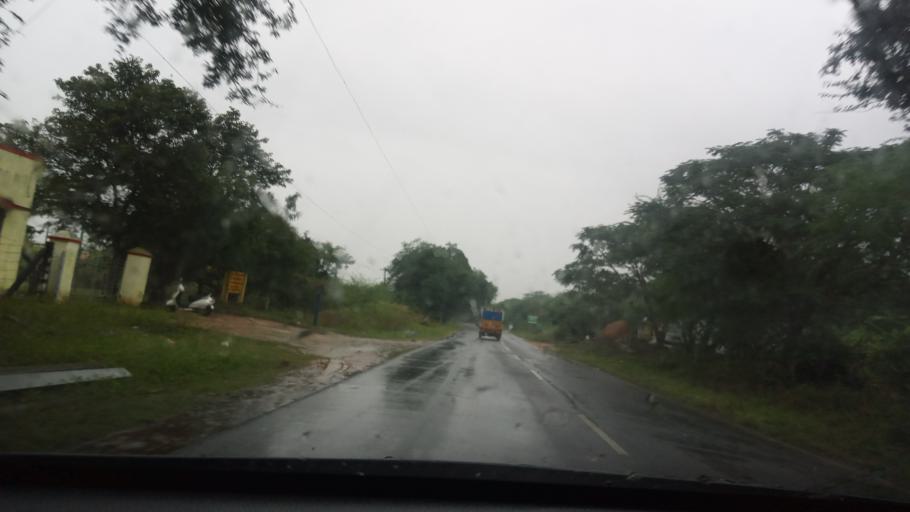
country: IN
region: Tamil Nadu
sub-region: Vellore
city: Walajapet
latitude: 12.8604
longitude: 79.3774
